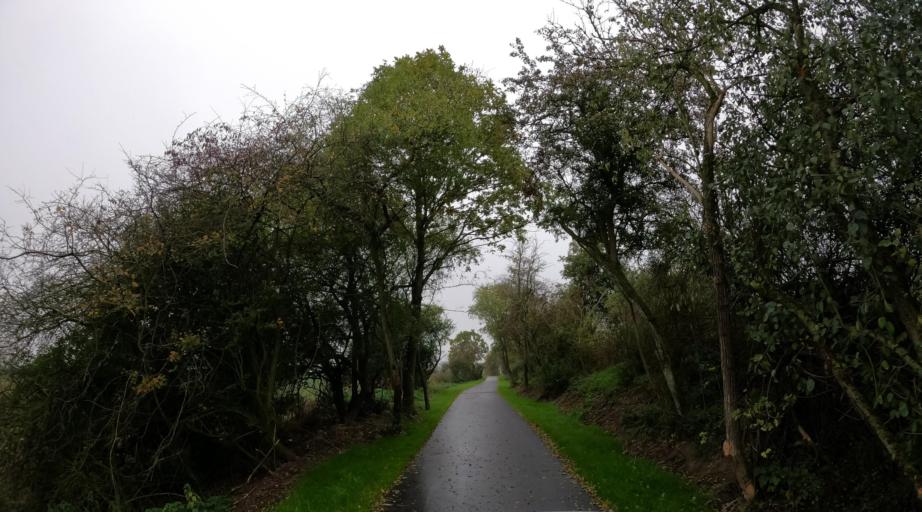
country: PL
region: West Pomeranian Voivodeship
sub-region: Powiat mysliborski
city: Mysliborz
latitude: 52.9084
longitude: 14.7476
